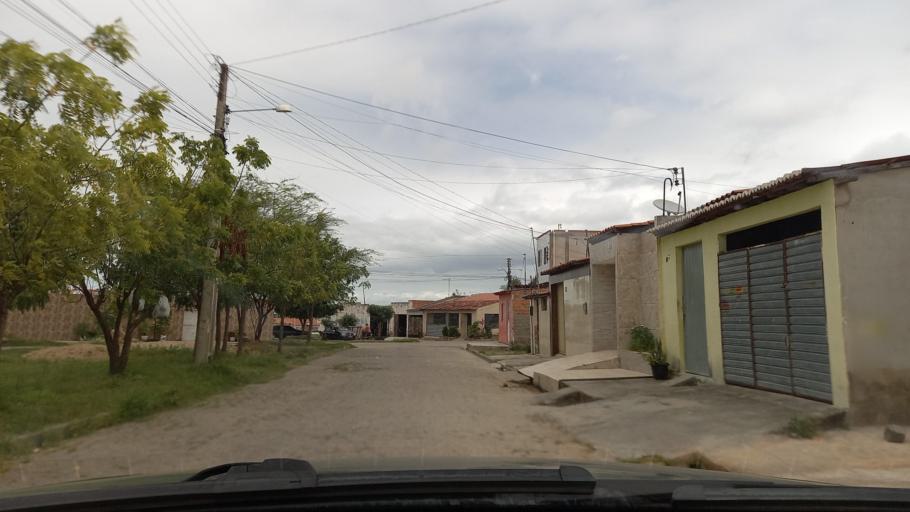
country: BR
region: Sergipe
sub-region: Caninde De Sao Francisco
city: Caninde de Sao Francisco
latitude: -9.6103
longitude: -37.7602
